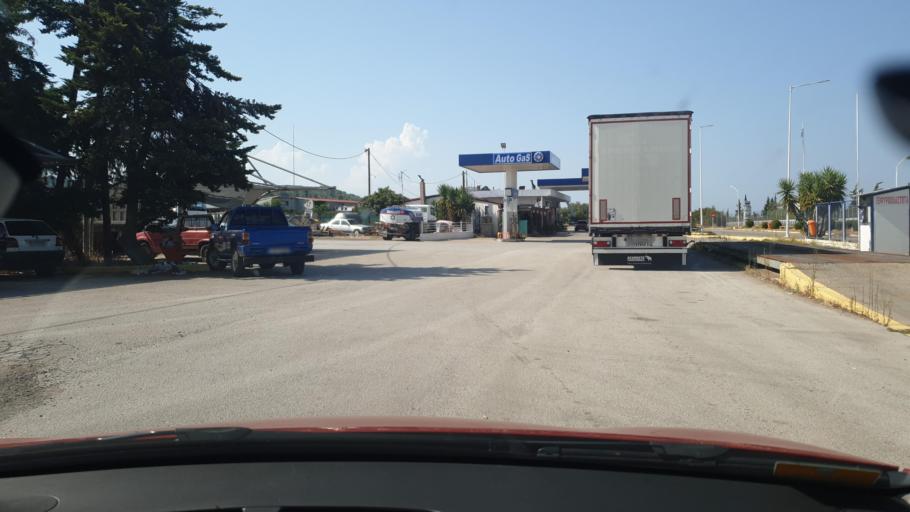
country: GR
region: Central Greece
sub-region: Nomos Fthiotidos
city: Livanates
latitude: 38.7224
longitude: 23.0514
